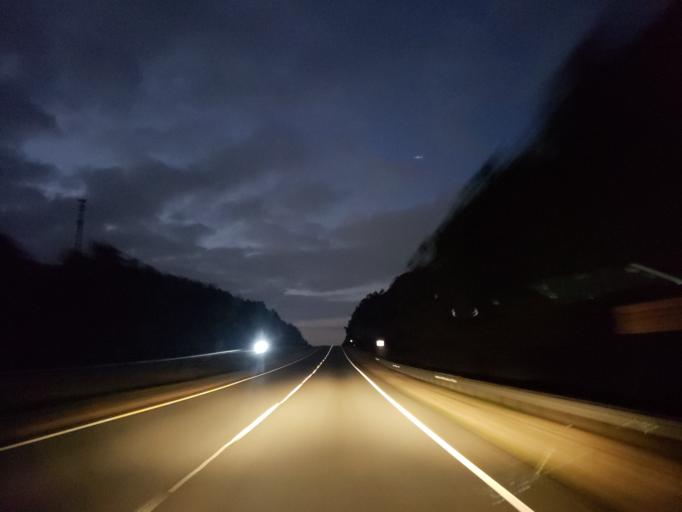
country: US
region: Georgia
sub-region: Polk County
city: Rockmart
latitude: 33.9764
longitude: -85.0065
